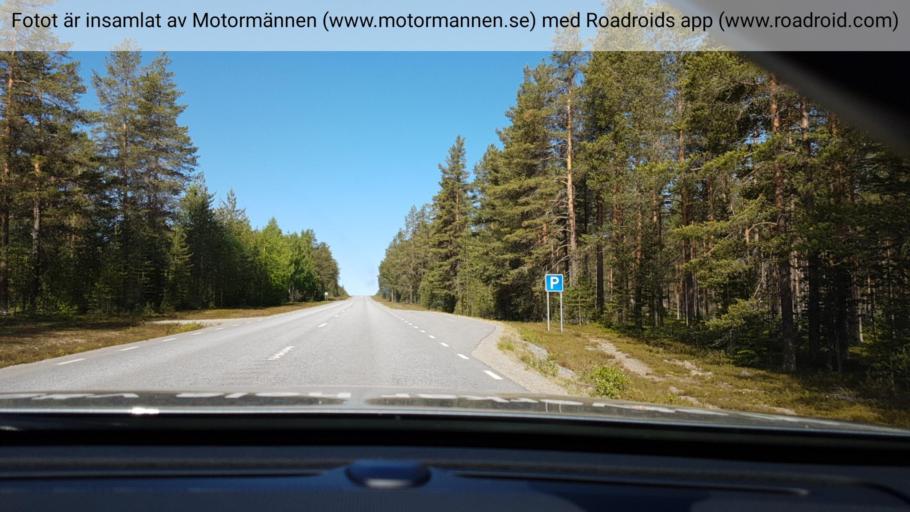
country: SE
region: Vaesterbotten
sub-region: Bjurholms Kommun
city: Bjurholm
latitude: 63.9296
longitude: 19.0009
